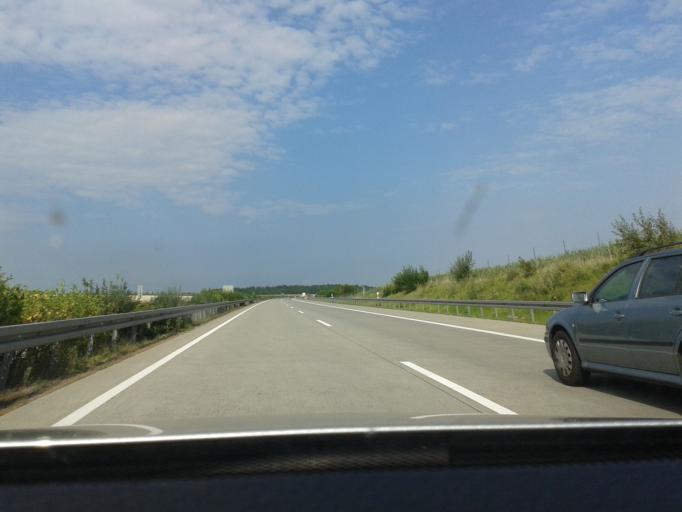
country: DE
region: Thuringia
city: Heilbad Heiligenstadt
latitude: 51.4009
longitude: 10.1369
